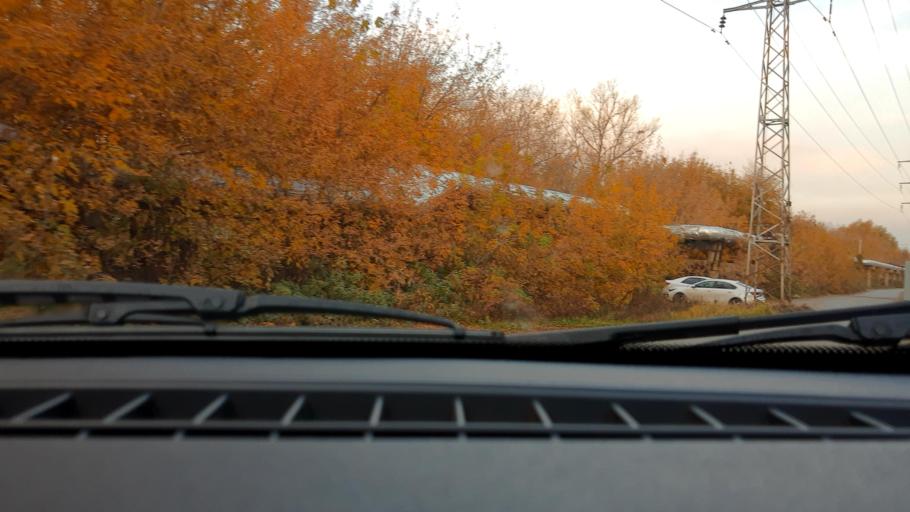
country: RU
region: Bashkortostan
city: Ufa
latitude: 54.7963
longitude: 56.1156
